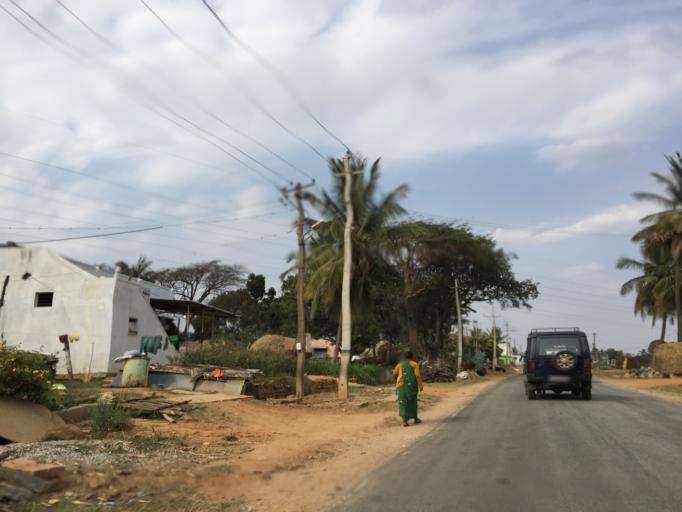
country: IN
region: Karnataka
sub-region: Chikkaballapur
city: Chik Ballapur
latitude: 13.3907
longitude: 77.6998
